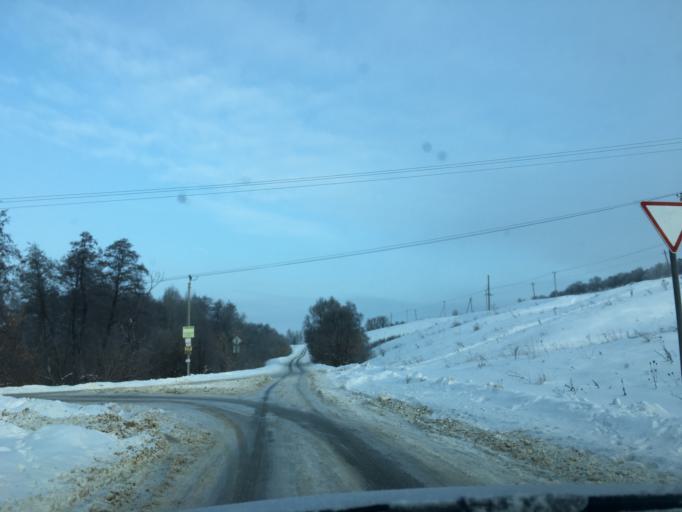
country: RU
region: Belgorod
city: Severnyy
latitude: 50.7267
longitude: 36.6121
